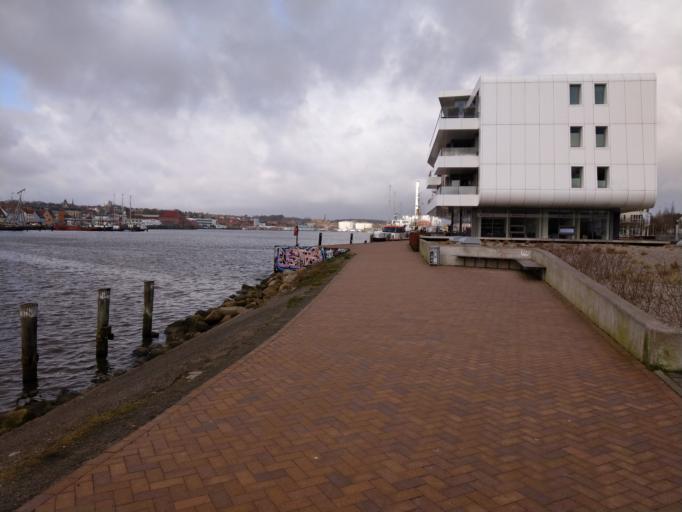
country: DE
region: Schleswig-Holstein
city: Flensburg
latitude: 54.7925
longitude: 9.4379
